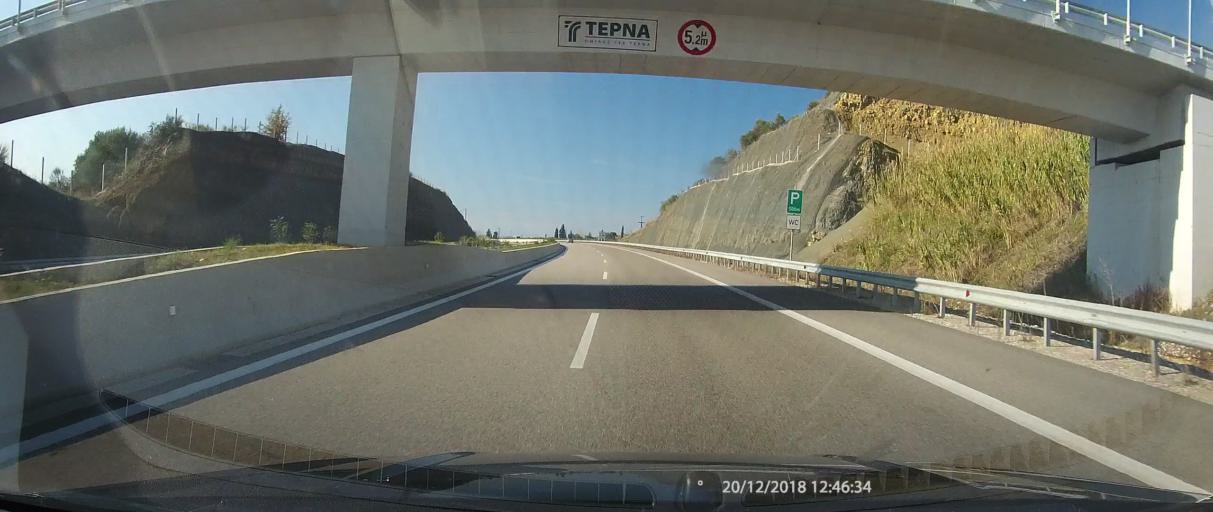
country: GR
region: West Greece
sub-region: Nomos Aitolias kai Akarnanias
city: Mesolongi
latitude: 38.3931
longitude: 21.4703
